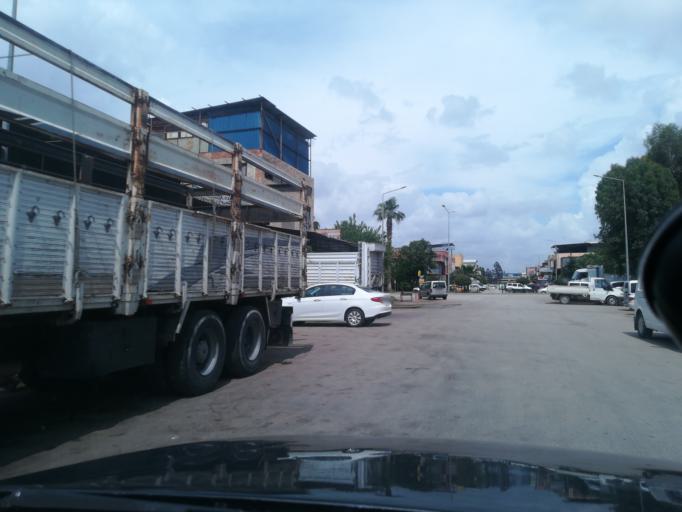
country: TR
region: Adana
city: Seyhan
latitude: 36.9825
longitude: 35.2547
